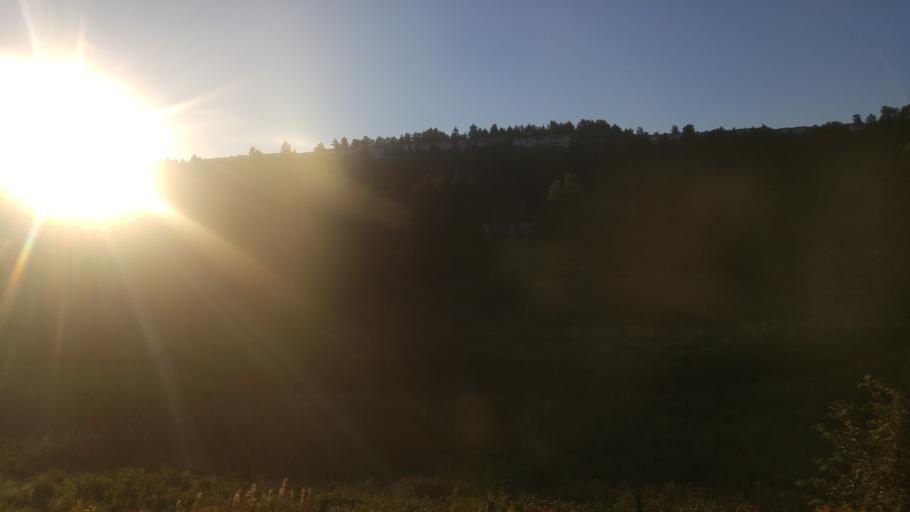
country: NO
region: Oslo
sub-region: Oslo
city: Oslo
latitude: 59.9180
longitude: 10.8303
